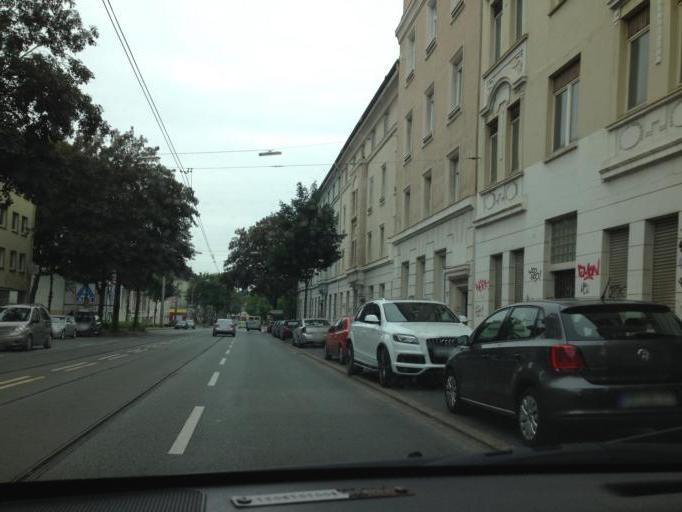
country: DE
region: North Rhine-Westphalia
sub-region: Regierungsbezirk Arnsberg
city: Dortmund
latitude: 51.5123
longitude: 7.4360
